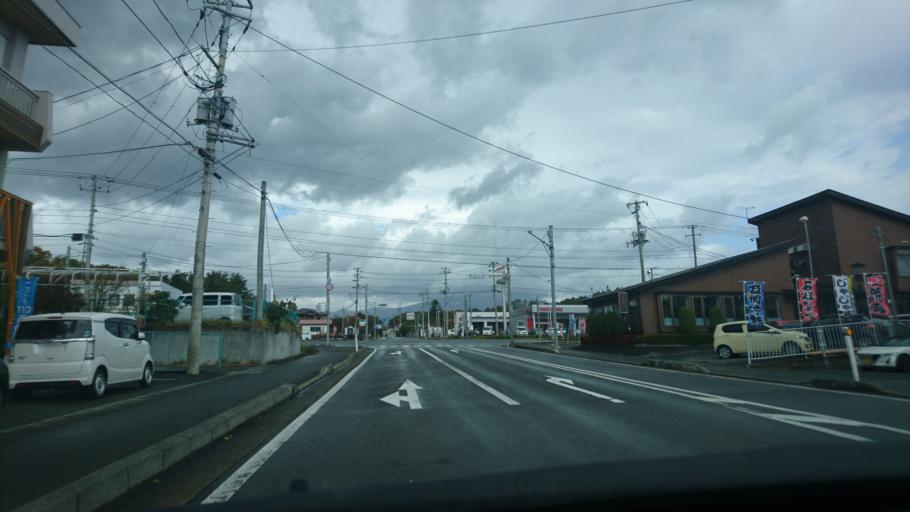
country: JP
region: Iwate
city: Shizukuishi
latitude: 39.6973
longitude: 141.0229
